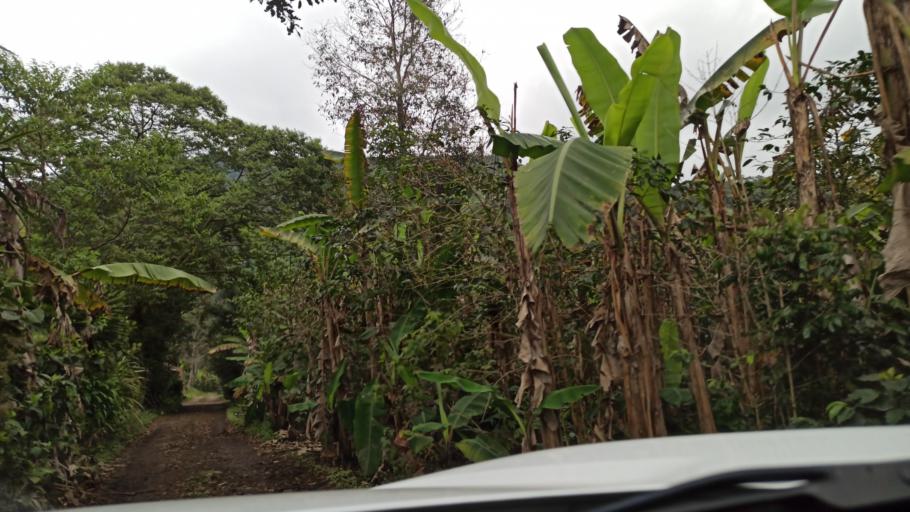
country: MX
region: Veracruz
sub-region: Fortin
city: Santa Lucia Potrerillo
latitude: 18.9746
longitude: -97.0335
